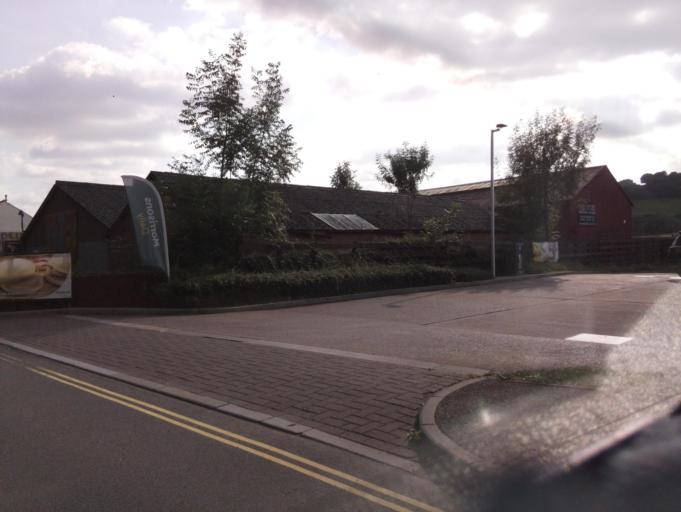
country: GB
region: England
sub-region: Devon
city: Exeter
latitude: 50.7384
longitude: -3.5450
